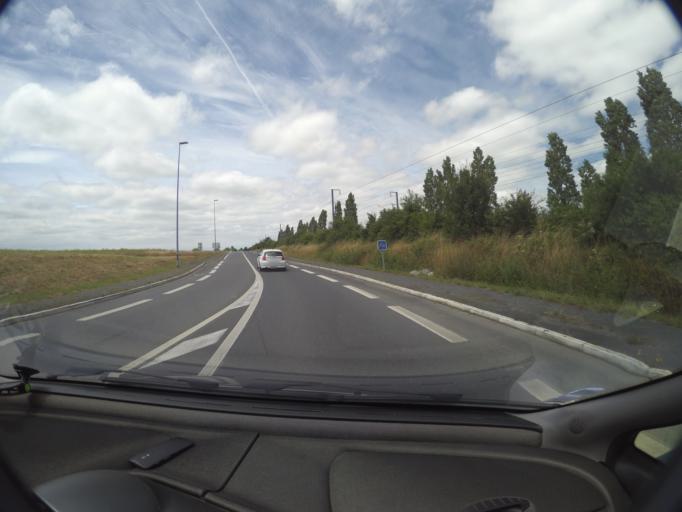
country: FR
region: Pays de la Loire
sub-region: Departement de la Loire-Atlantique
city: Gorges
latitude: 47.0951
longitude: -1.2995
